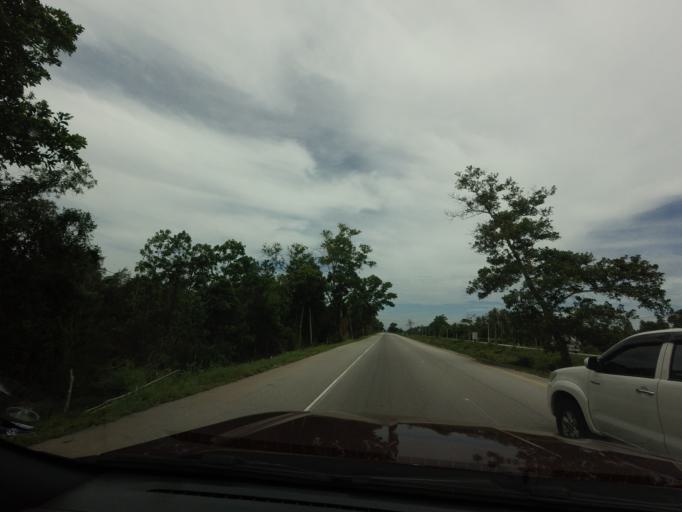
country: TH
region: Narathiwat
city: Narathiwat
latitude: 6.3598
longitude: 101.9125
